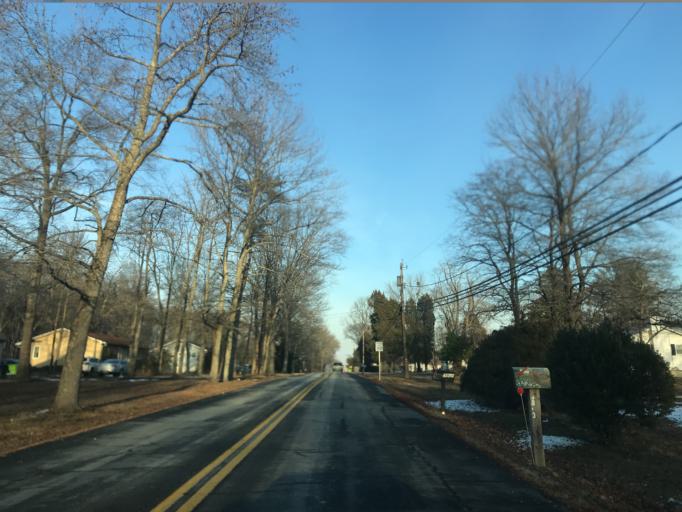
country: US
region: Maryland
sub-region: Harford County
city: Riverside
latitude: 39.4353
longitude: -76.2546
